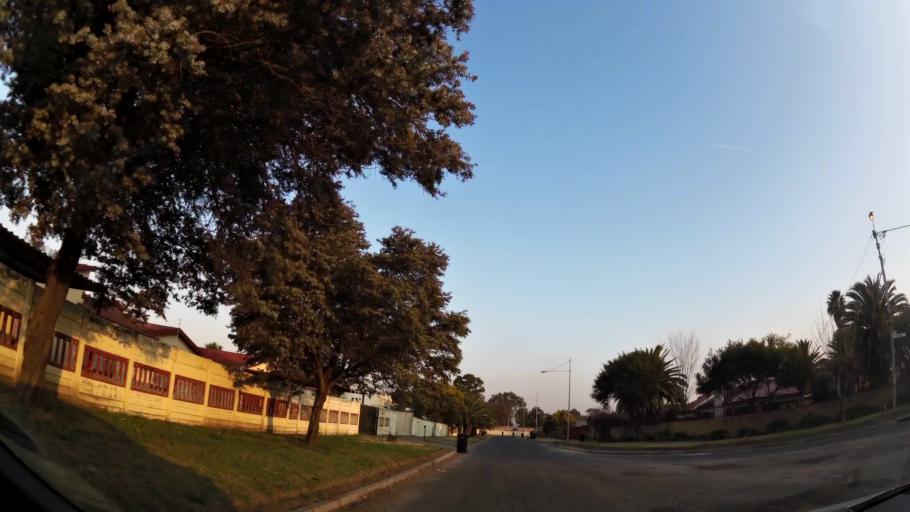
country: ZA
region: Gauteng
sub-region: Ekurhuleni Metropolitan Municipality
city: Springs
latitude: -26.3120
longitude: 28.4532
